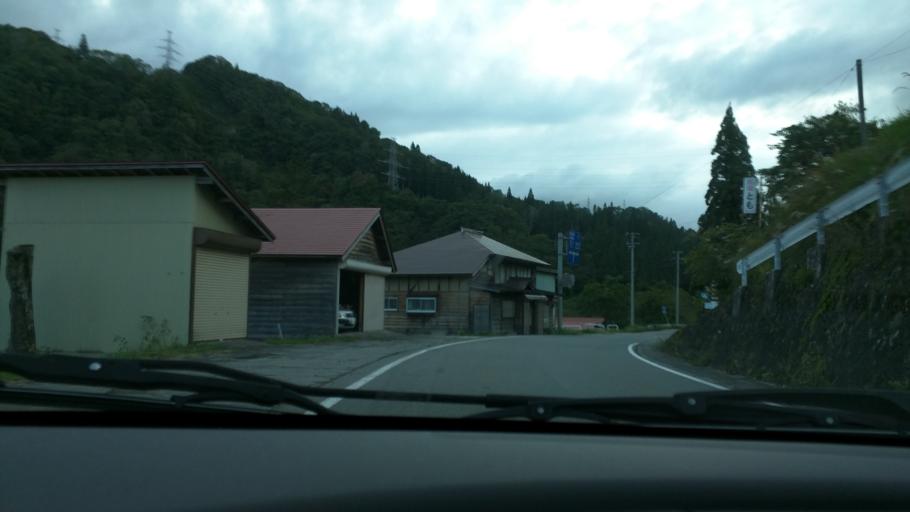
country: JP
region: Fukushima
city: Kitakata
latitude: 37.4384
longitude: 139.5275
